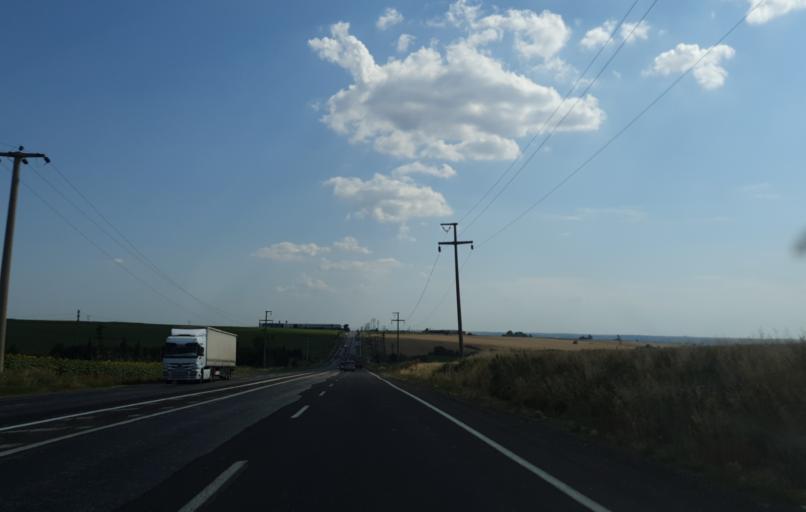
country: TR
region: Kirklareli
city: Buyukkaristiran
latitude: 41.2644
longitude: 27.5489
